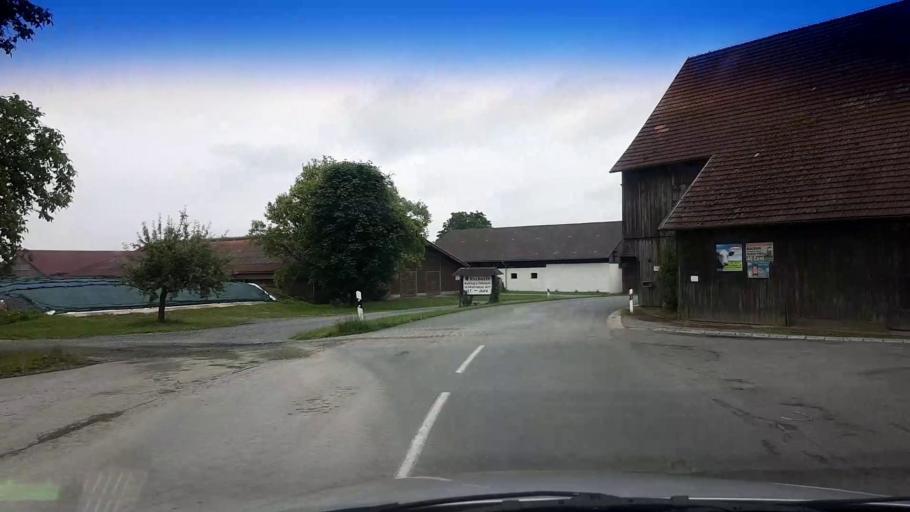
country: DE
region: Bavaria
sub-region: Upper Franconia
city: Kasendorf
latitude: 50.0806
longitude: 11.3161
